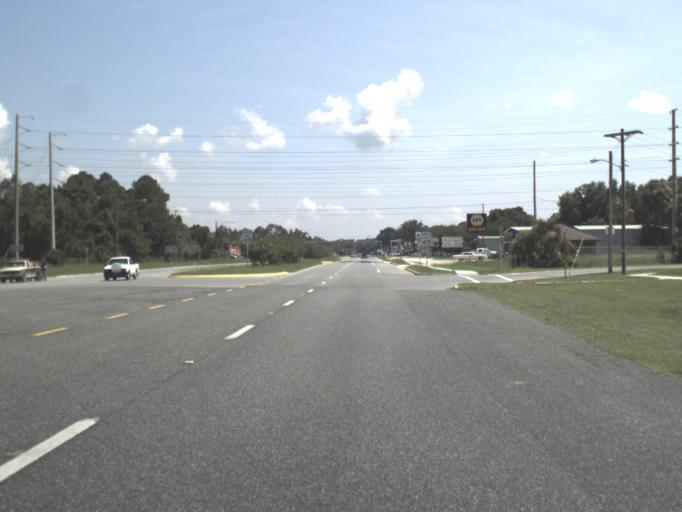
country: US
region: Florida
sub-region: Levy County
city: Inglis
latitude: 29.0343
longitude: -82.6693
